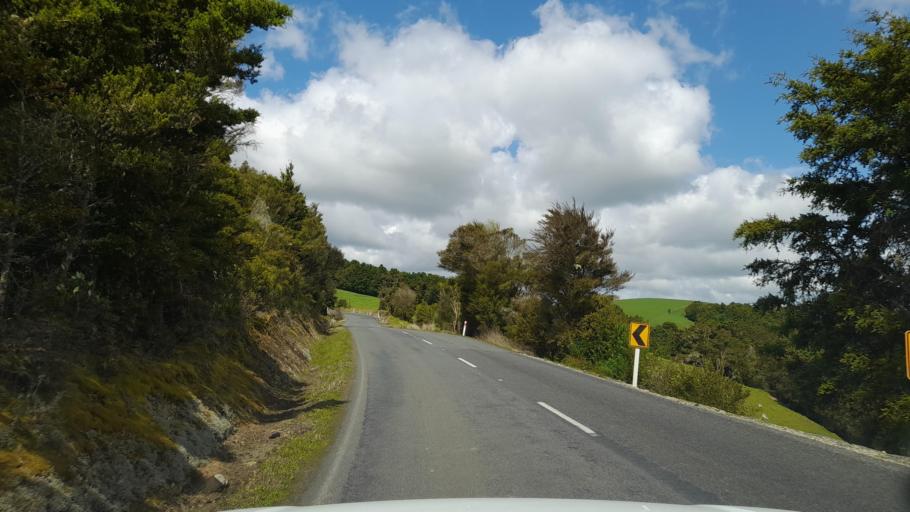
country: NZ
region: Northland
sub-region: Whangarei
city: Maungatapere
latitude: -35.6389
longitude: 174.0612
